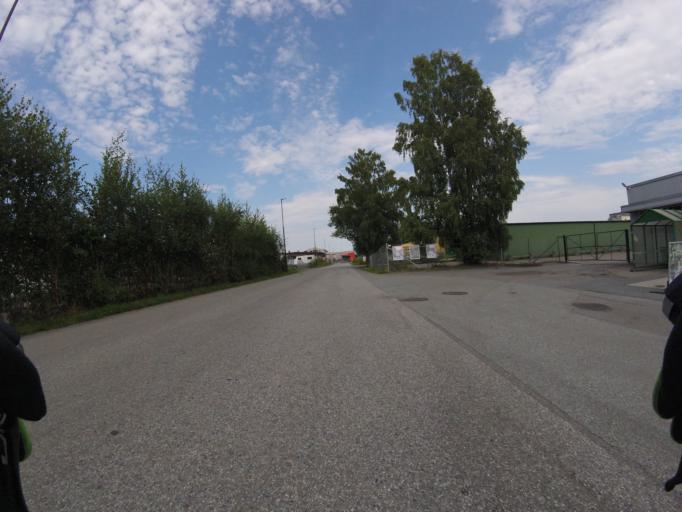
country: NO
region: Akershus
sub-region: Skedsmo
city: Lillestrom
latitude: 59.9482
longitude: 11.0665
